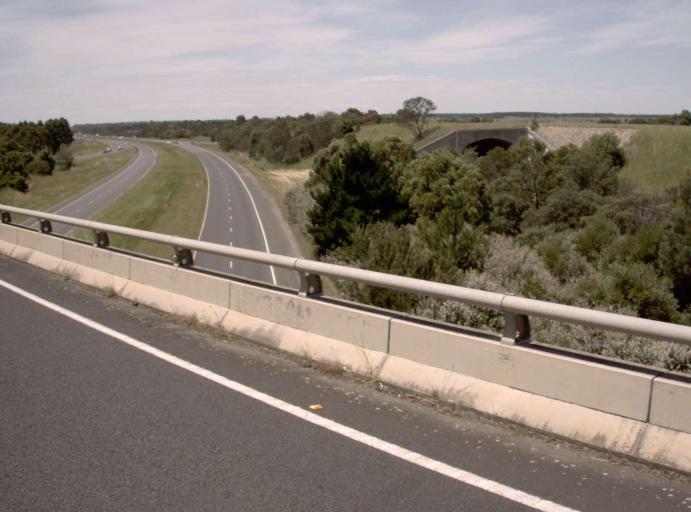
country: AU
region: Victoria
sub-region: Latrobe
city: Morwell
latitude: -38.2298
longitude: 146.4567
